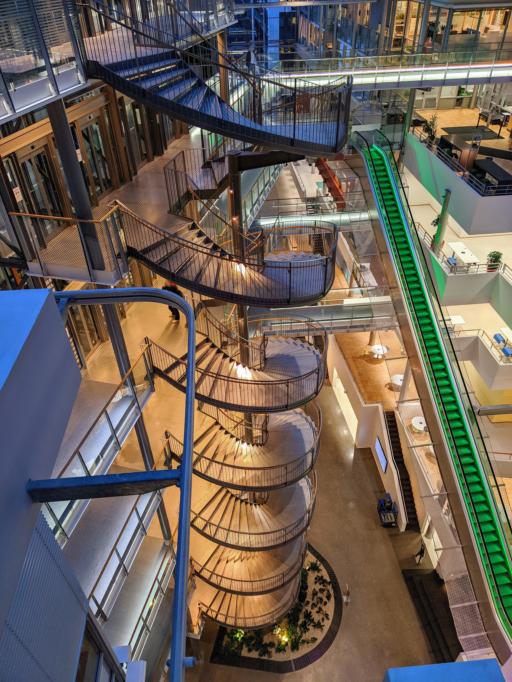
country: NO
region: Oslo
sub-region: Oslo
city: Oslo
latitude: 59.9486
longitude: 10.7683
